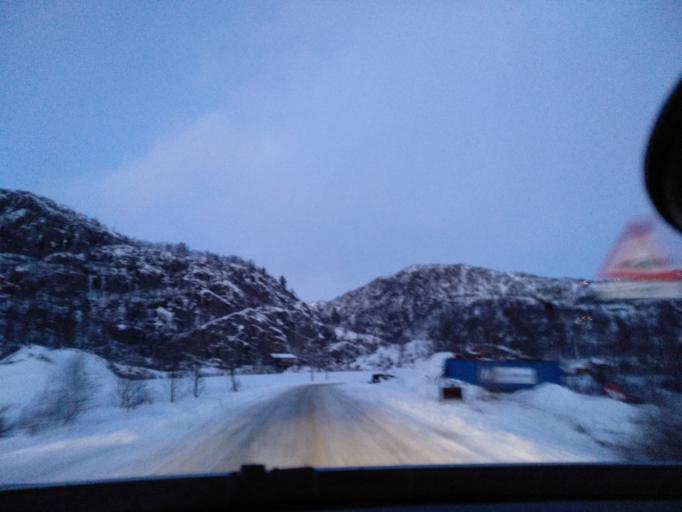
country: NO
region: Vest-Agder
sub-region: Sirdal
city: Tonstad
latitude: 59.0188
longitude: 6.9361
